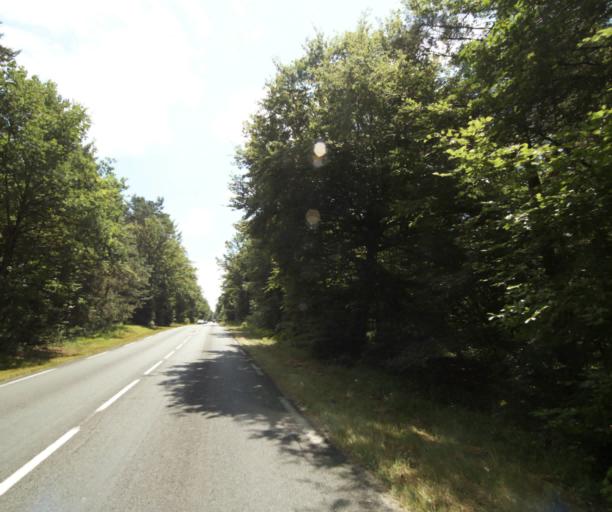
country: FR
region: Ile-de-France
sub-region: Departement de Seine-et-Marne
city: Bois-le-Roi
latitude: 48.4478
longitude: 2.7135
